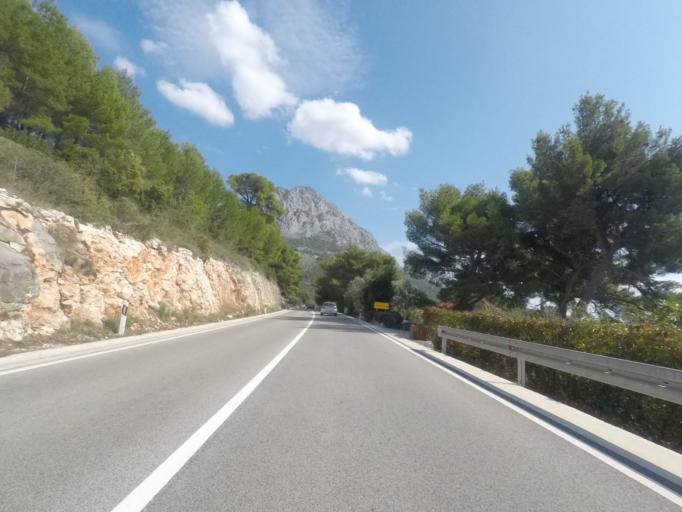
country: HR
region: Splitsko-Dalmatinska
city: Vrgorac
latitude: 43.1419
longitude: 17.2739
